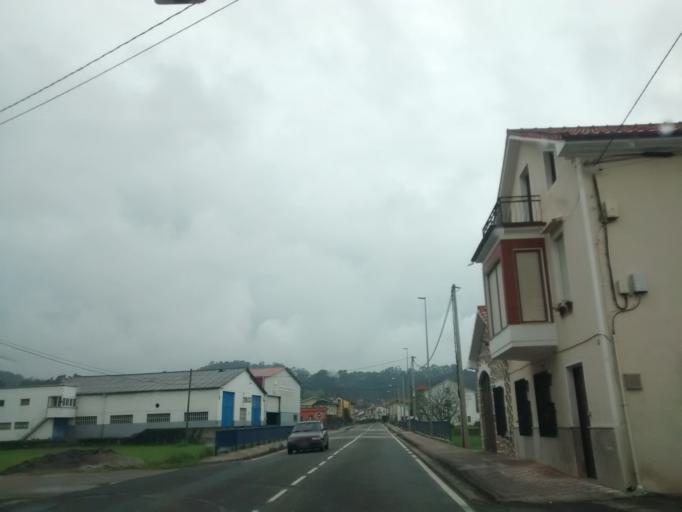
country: ES
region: Cantabria
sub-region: Provincia de Cantabria
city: Camargo
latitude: 43.4027
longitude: -3.8781
